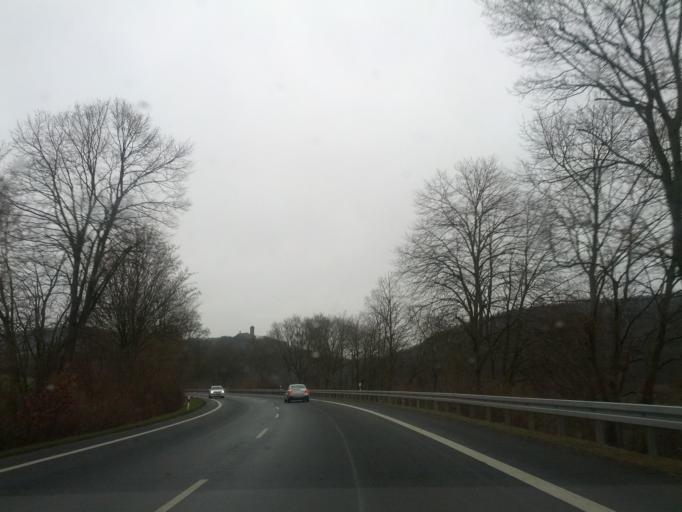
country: DE
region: Hesse
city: Witzenhausen
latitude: 51.3215
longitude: 9.8906
